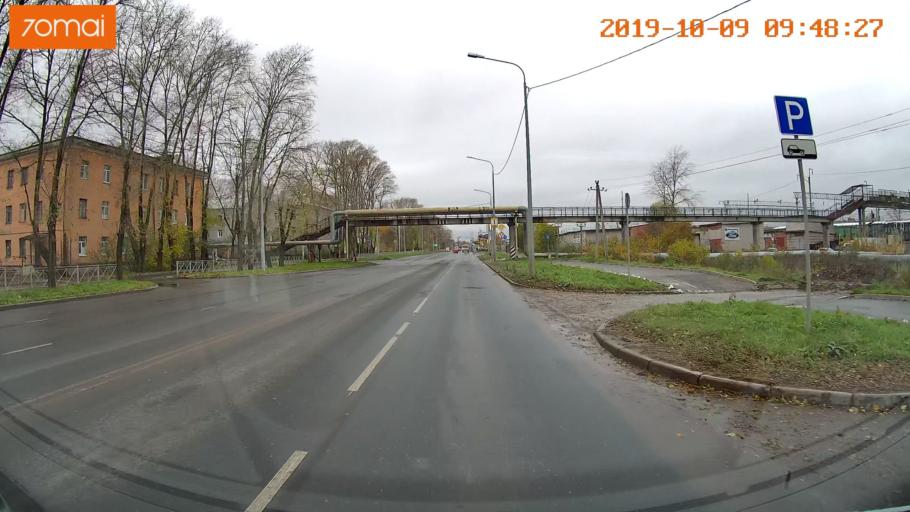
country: RU
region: Vologda
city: Vologda
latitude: 59.1945
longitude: 39.9285
